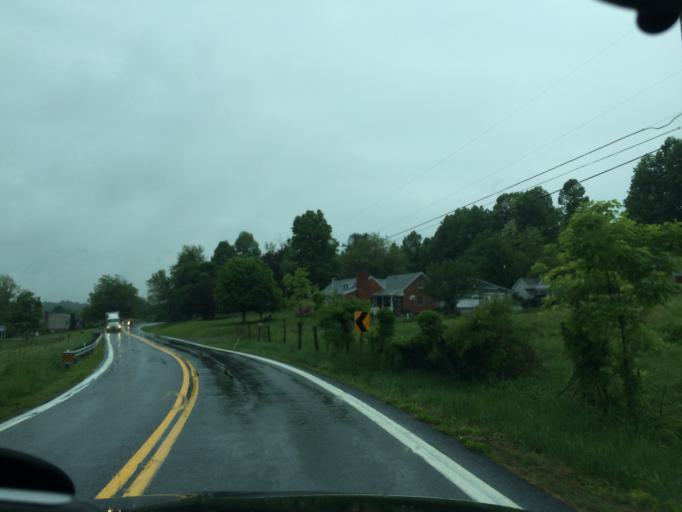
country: US
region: Maryland
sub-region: Washington County
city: Highfield-Cascade
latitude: 39.6960
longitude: -77.4866
